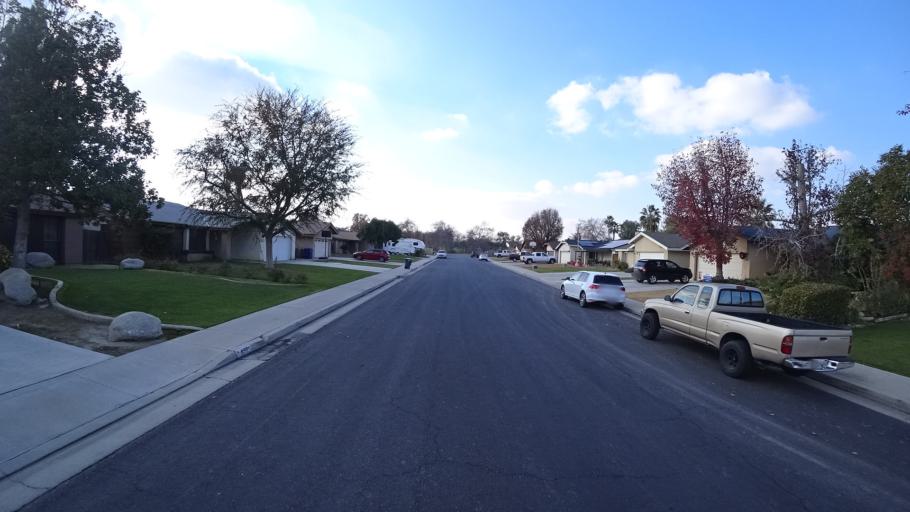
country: US
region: California
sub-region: Kern County
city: Greenacres
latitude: 35.3151
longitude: -119.0975
